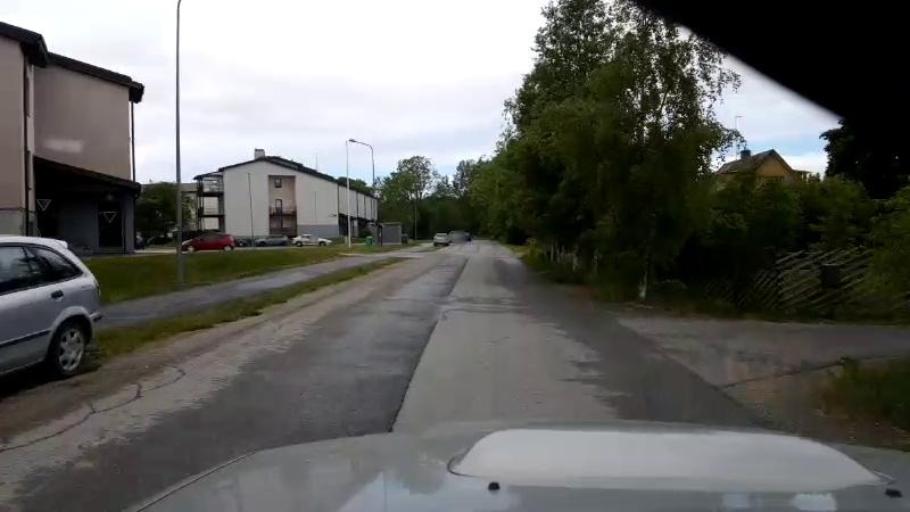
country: EE
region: Harju
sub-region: Harku vald
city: Tabasalu
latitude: 59.4561
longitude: 24.4347
